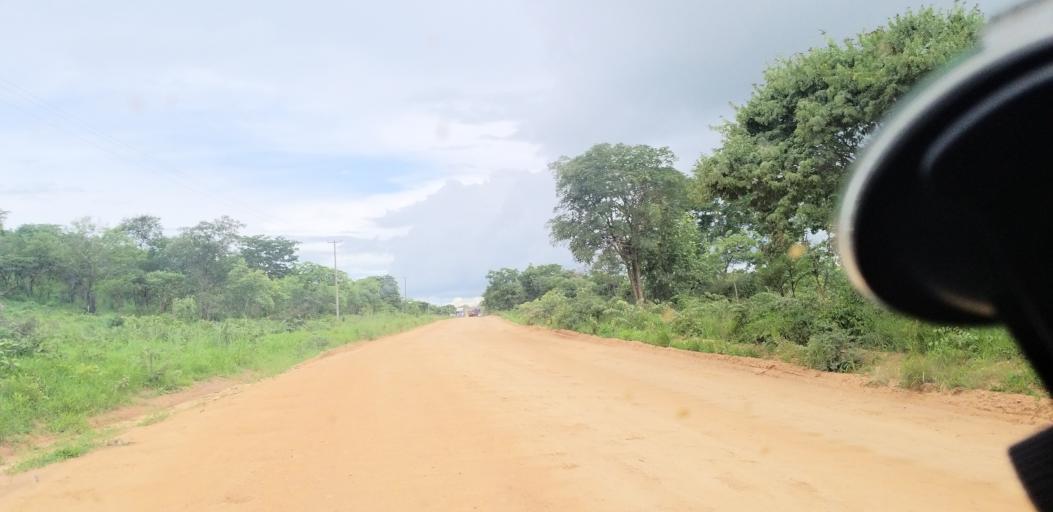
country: ZM
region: Lusaka
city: Chongwe
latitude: -15.1800
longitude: 28.4519
